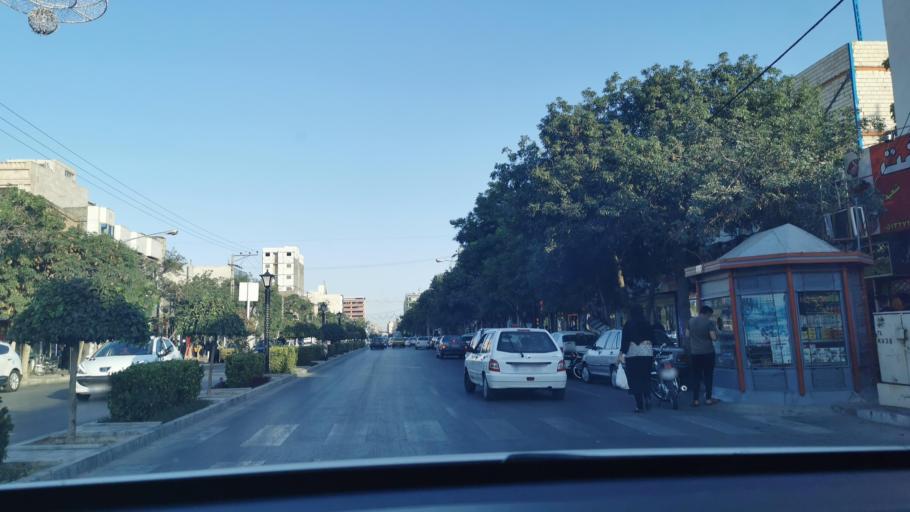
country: IR
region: Razavi Khorasan
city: Mashhad
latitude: 36.2958
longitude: 59.6436
